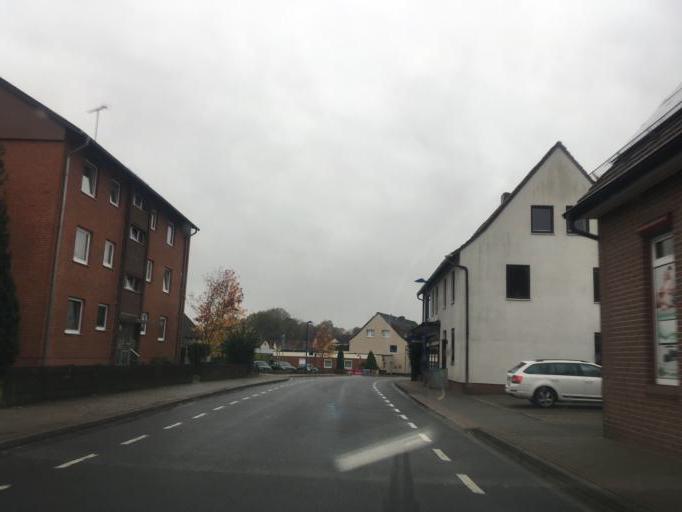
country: DE
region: Lower Saxony
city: Bergen
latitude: 52.8091
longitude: 9.9675
